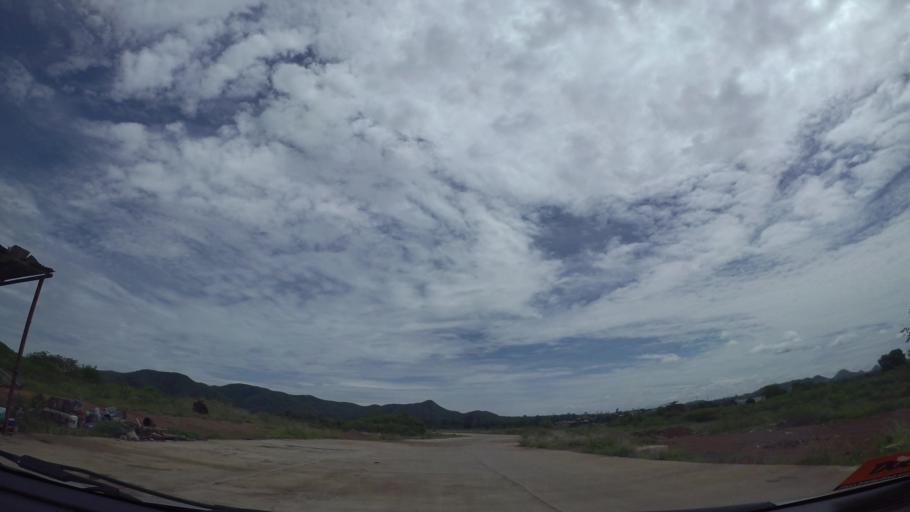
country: TH
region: Chon Buri
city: Sattahip
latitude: 12.6927
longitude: 100.8843
